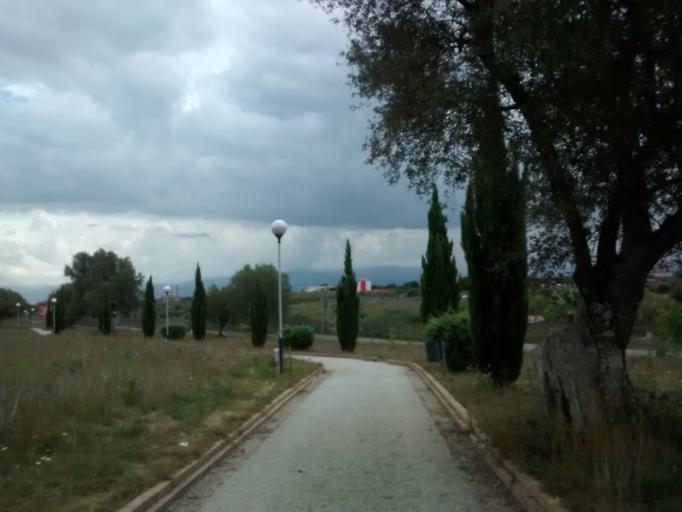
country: IT
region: Calabria
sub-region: Provincia di Vibo-Valentia
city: Vibo Valentia
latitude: 38.6629
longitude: 16.0771
